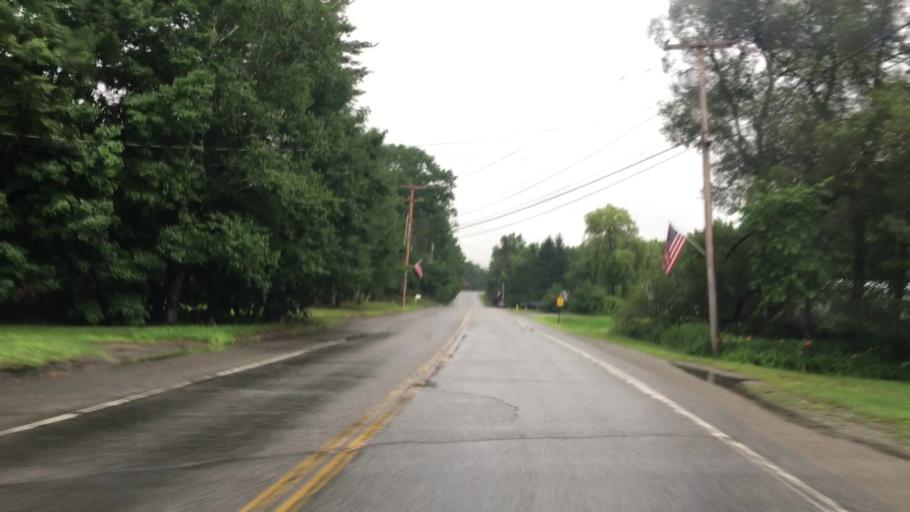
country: US
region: Maine
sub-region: Kennebec County
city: Pittston
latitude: 44.1939
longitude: -69.7600
